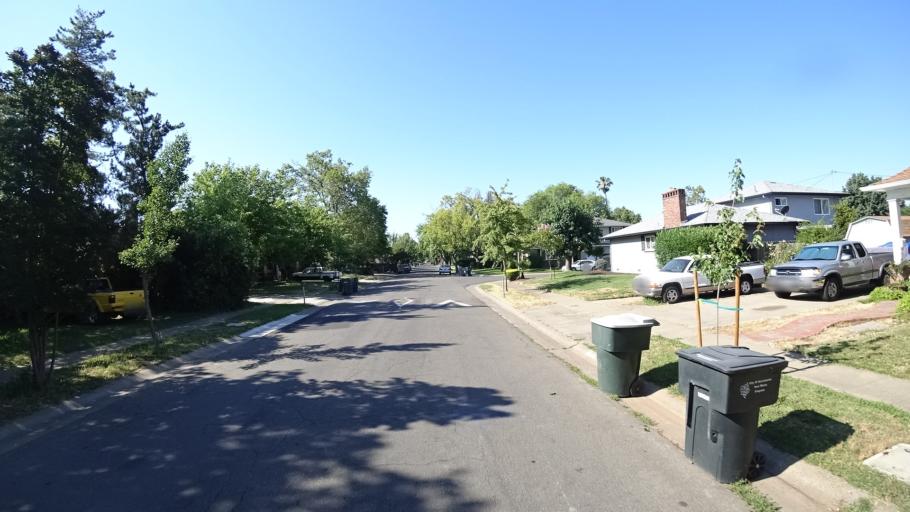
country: US
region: California
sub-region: Sacramento County
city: Florin
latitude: 38.5373
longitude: -121.4237
